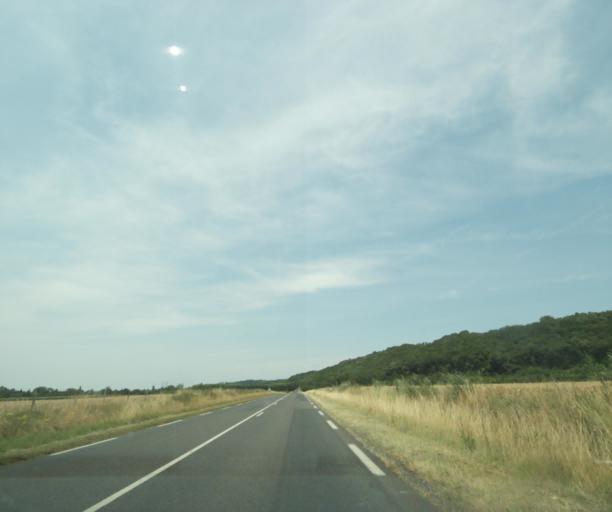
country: FR
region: Poitou-Charentes
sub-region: Departement de la Vienne
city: Bonneuil-Matours
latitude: 46.6641
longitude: 0.5804
